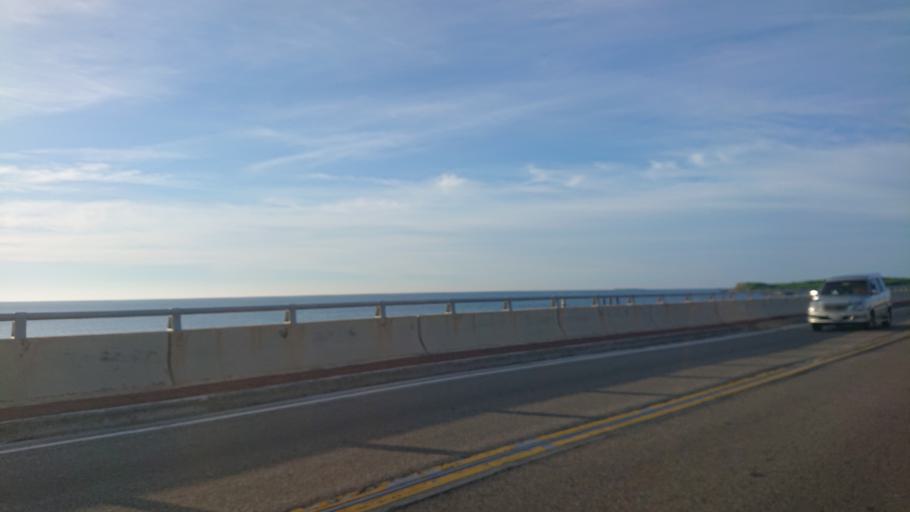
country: TW
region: Taiwan
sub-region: Penghu
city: Ma-kung
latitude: 23.6495
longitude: 119.5472
